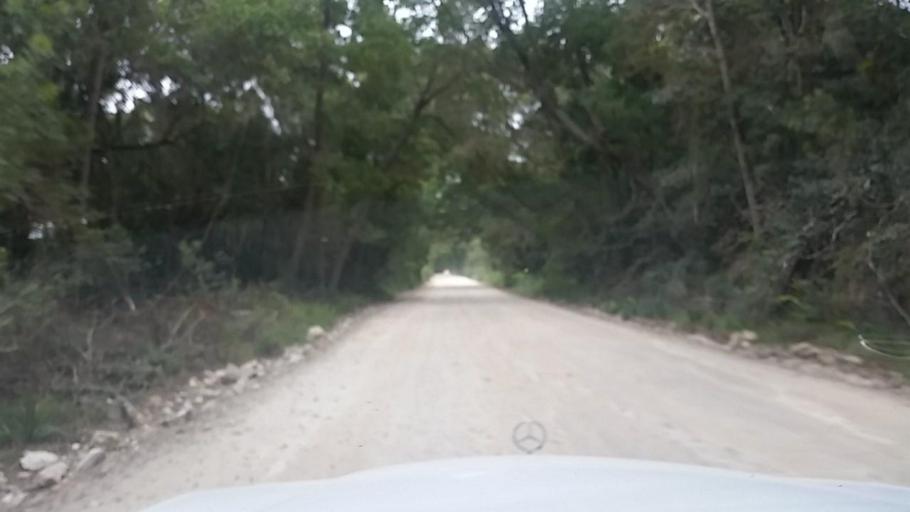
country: ZA
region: Western Cape
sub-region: Eden District Municipality
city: Knysna
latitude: -33.9766
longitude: 23.1414
